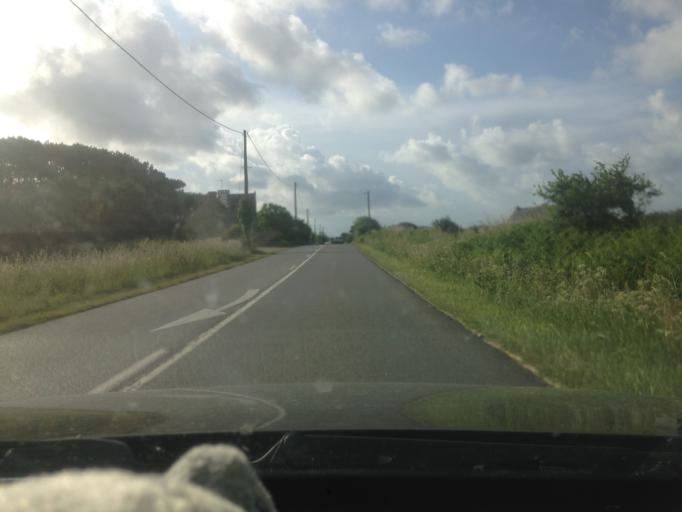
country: FR
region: Brittany
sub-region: Departement du Morbihan
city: Plouharnel
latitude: 47.5948
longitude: -3.1045
